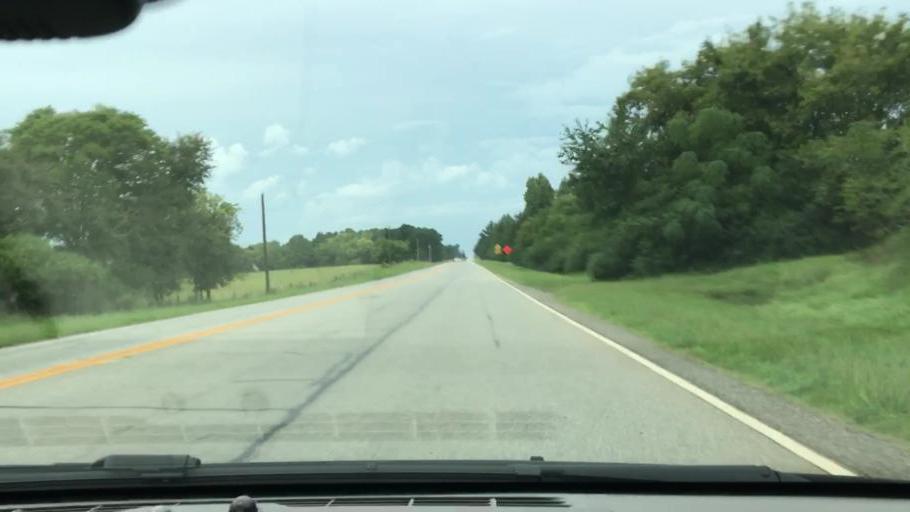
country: US
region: Georgia
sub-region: Early County
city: Blakely
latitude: 31.3311
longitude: -84.9972
